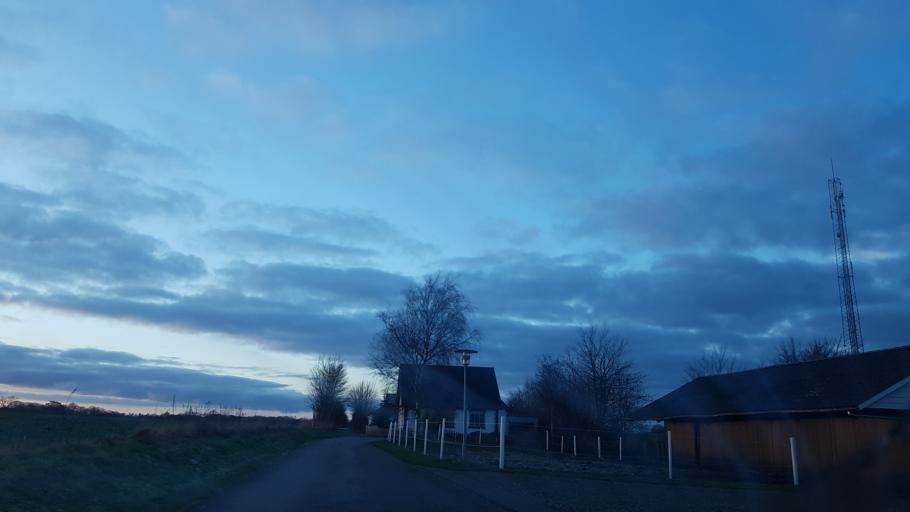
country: DK
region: South Denmark
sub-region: Kolding Kommune
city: Vamdrup
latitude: 55.3433
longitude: 9.2486
